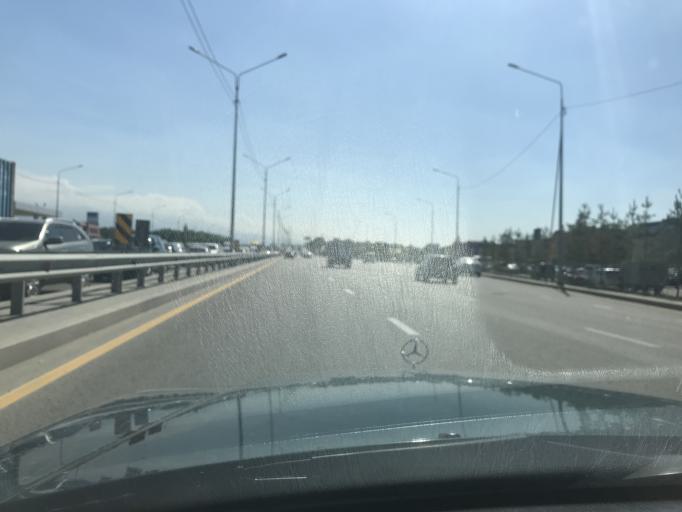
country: KZ
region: Almaty Qalasy
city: Almaty
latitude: 43.2998
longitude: 77.0044
